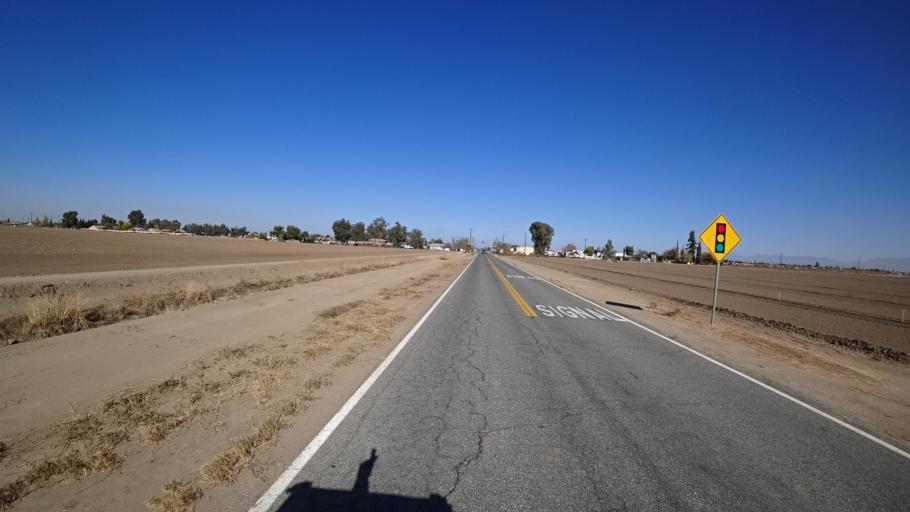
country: US
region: California
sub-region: Kern County
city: Greenfield
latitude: 35.2649
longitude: -119.0567
